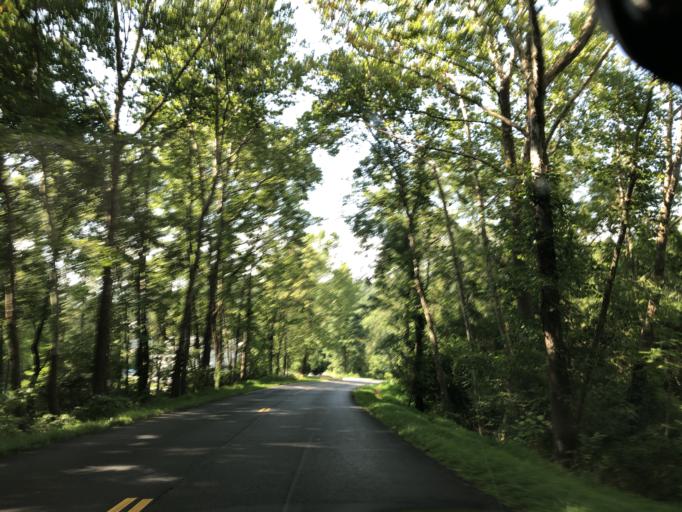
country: US
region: Maryland
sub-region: Frederick County
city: Linganore
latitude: 39.4263
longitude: -77.1799
